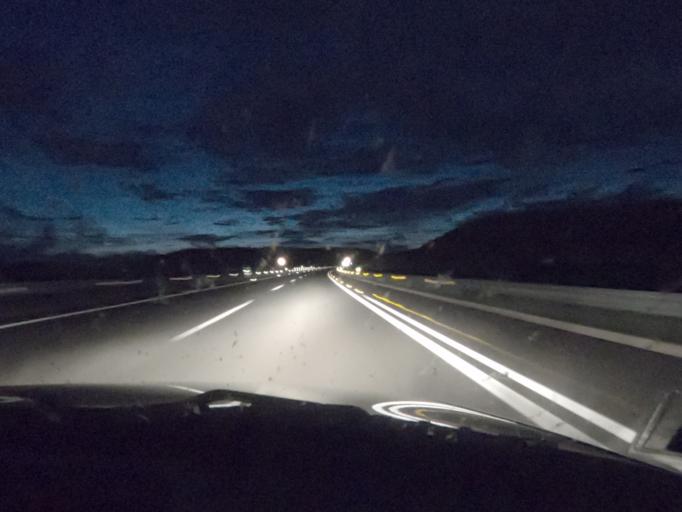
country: ES
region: Extremadura
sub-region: Provincia de Caceres
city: Coria
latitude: 39.9856
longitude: -6.5083
